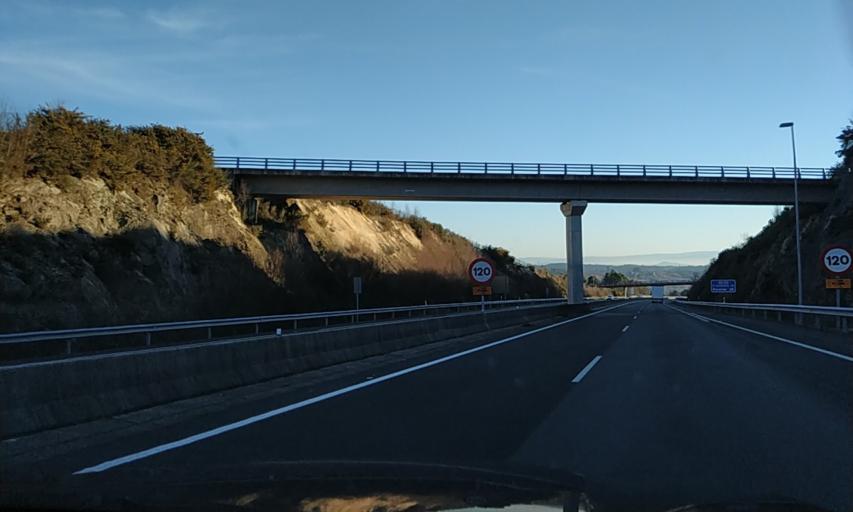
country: ES
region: Galicia
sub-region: Provincia de Ourense
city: Pinor
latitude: 42.5198
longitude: -8.0195
